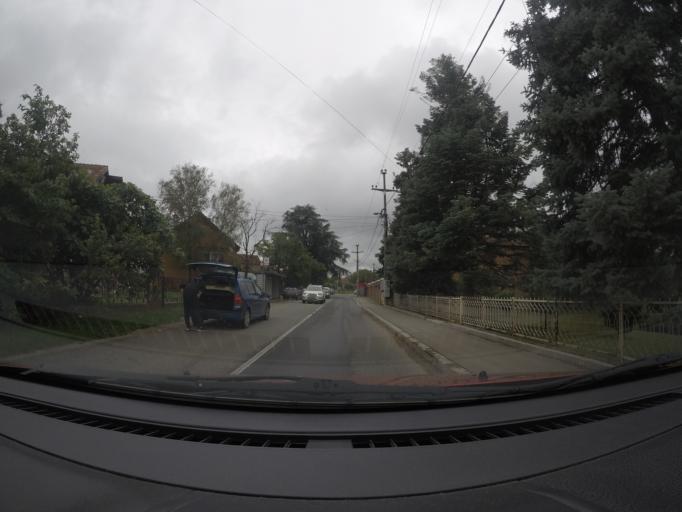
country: RS
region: Central Serbia
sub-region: Belgrade
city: Zvezdara
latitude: 44.6912
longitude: 20.5527
